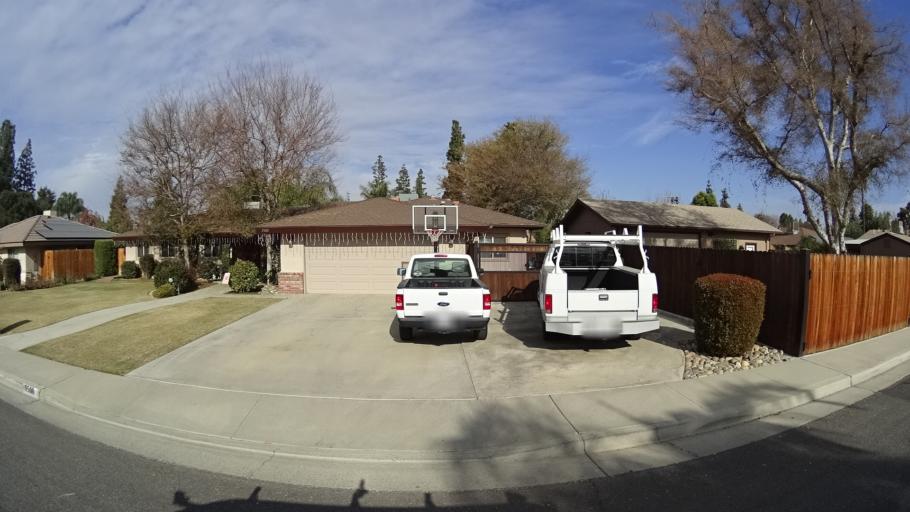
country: US
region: California
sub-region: Kern County
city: Greenacres
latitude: 35.4094
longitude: -119.0857
